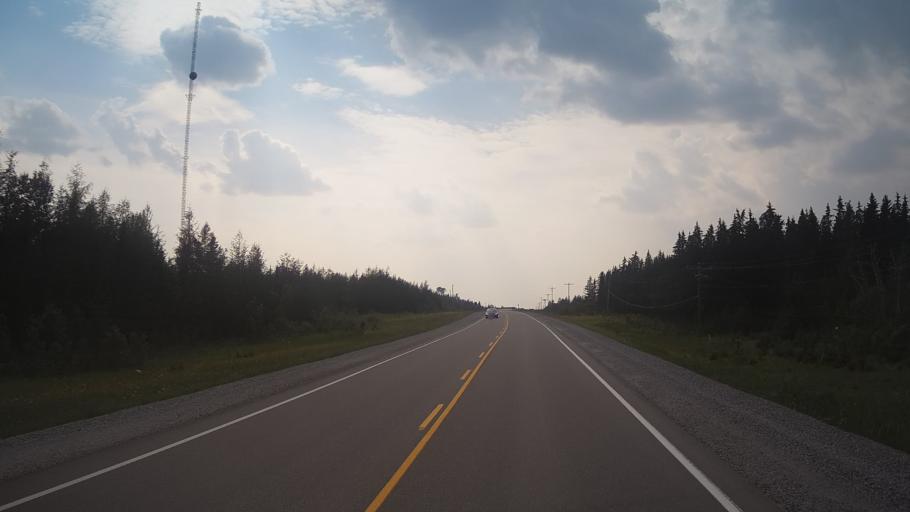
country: CA
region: Ontario
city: Kapuskasing
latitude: 49.5504
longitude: -82.9901
